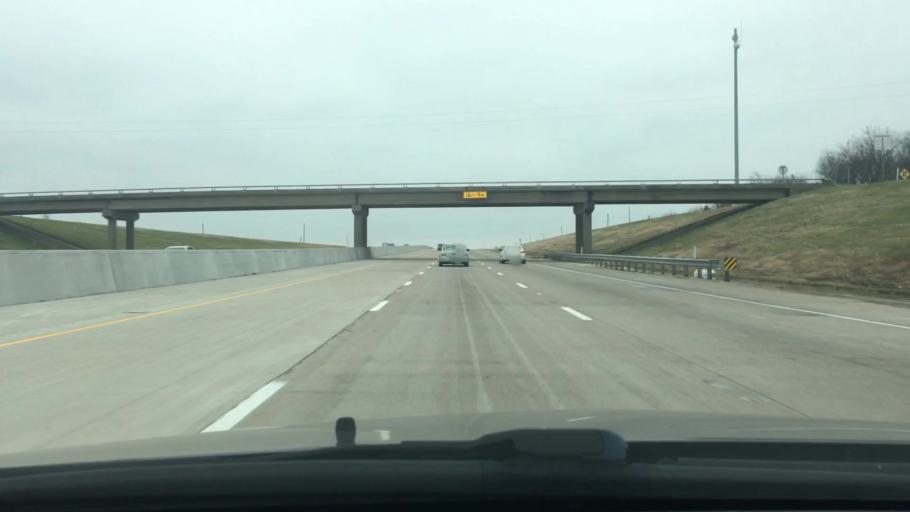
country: US
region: Texas
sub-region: Freestone County
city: Wortham
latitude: 31.9048
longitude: -96.3838
